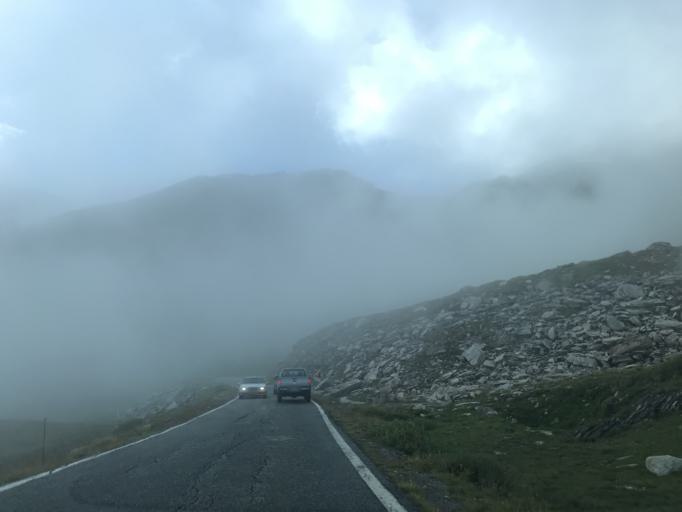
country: IT
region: Piedmont
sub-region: Provincia di Cuneo
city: Pontechianale
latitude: 44.6798
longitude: 6.9849
